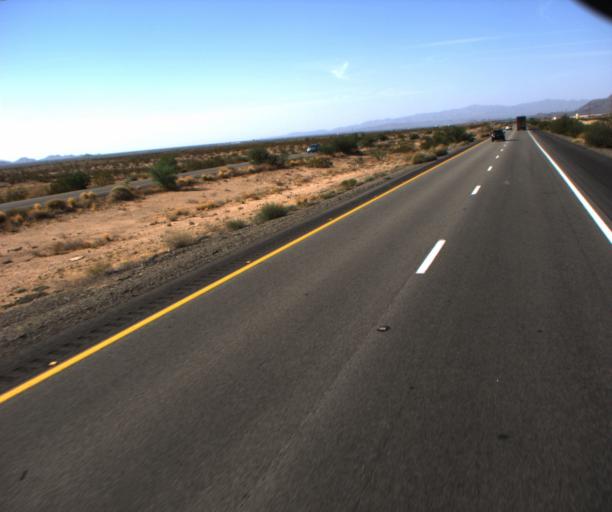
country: US
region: Arizona
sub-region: Mohave County
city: Kingman
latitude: 34.9283
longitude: -114.1502
